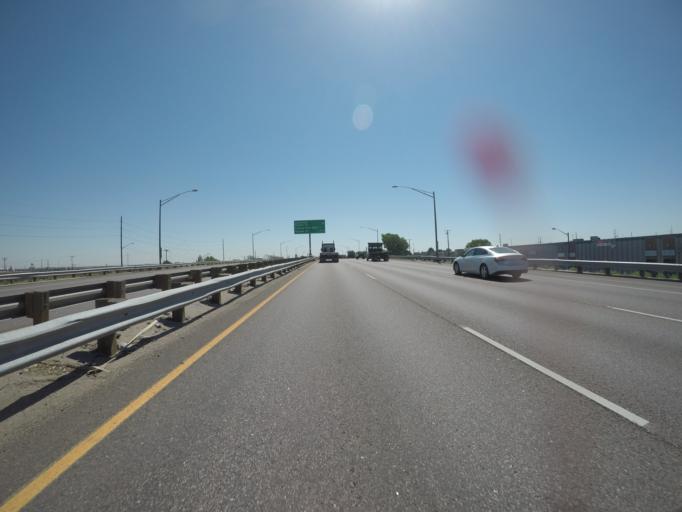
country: US
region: Colorado
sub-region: Adams County
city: Commerce City
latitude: 39.7783
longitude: -104.9142
